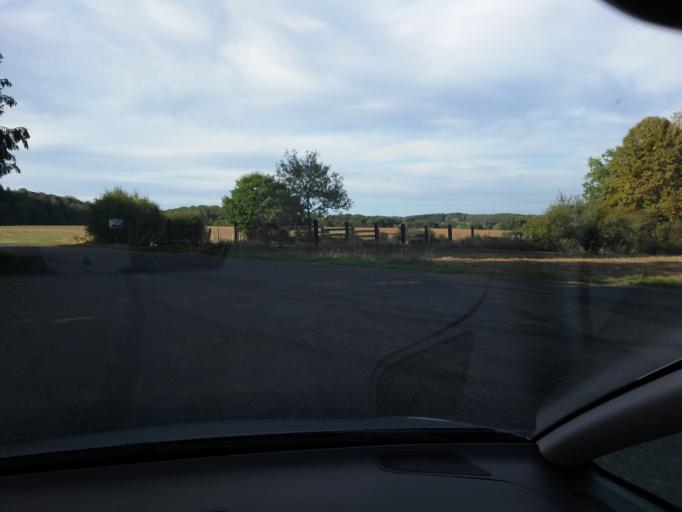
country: BE
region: Wallonia
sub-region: Province du Luxembourg
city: Attert
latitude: 49.7423
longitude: 5.7254
